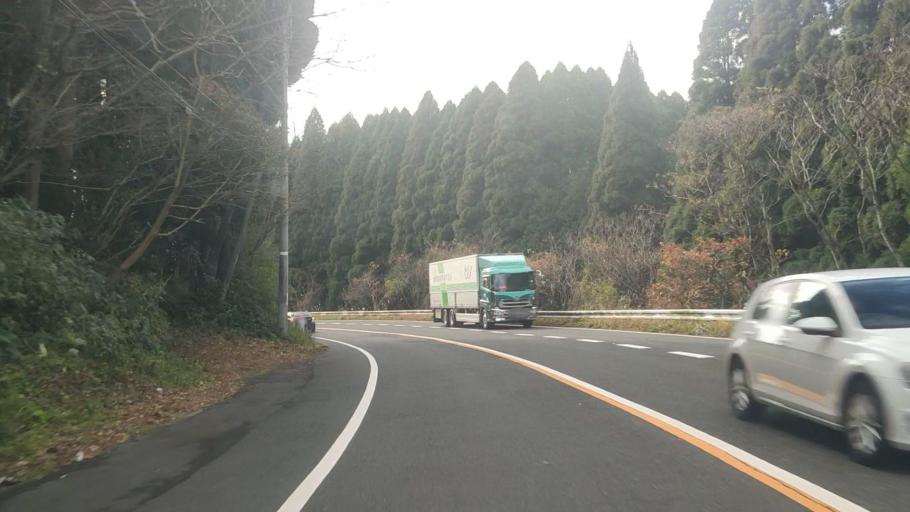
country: JP
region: Kagoshima
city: Kajiki
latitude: 31.7637
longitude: 130.6817
